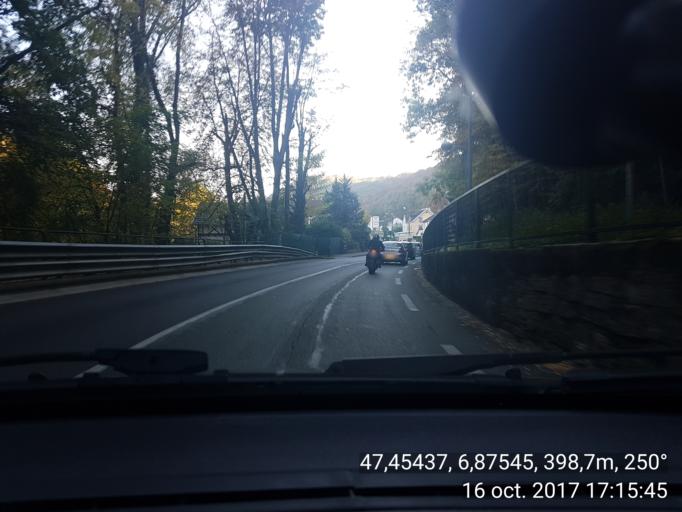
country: FR
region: Franche-Comte
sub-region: Departement du Doubs
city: Herimoncourt
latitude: 47.4544
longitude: 6.8754
